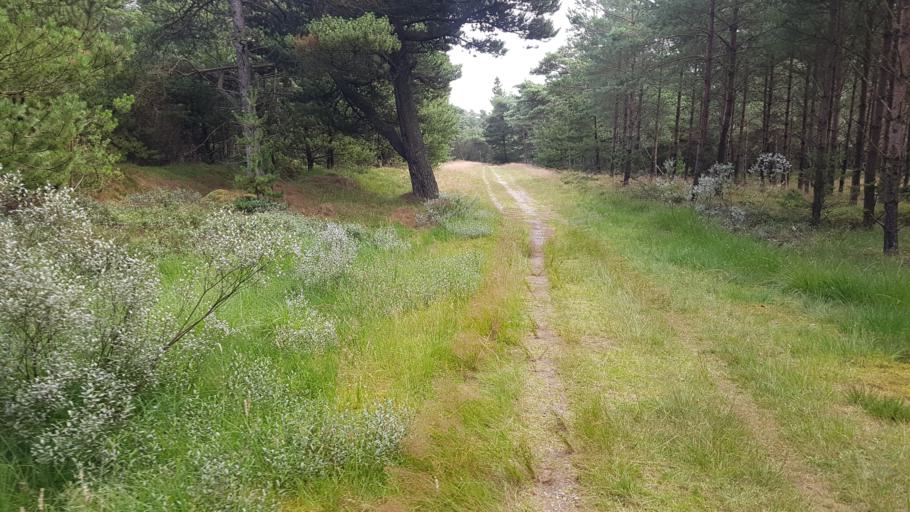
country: DE
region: Schleswig-Holstein
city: List
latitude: 55.1057
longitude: 8.5274
